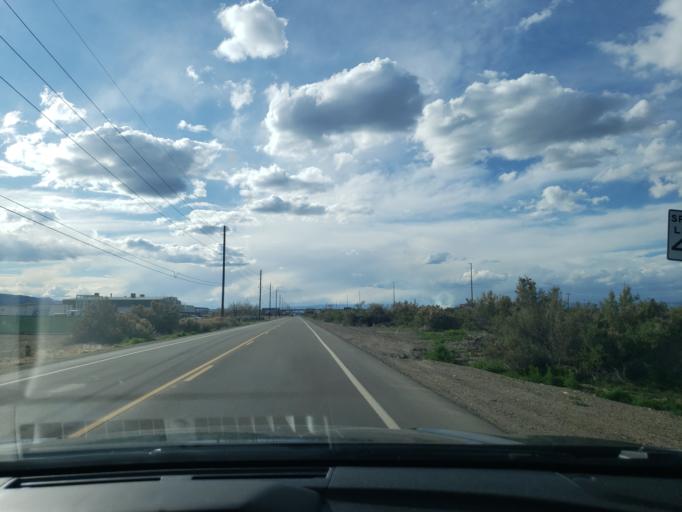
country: US
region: Colorado
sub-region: Mesa County
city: Redlands
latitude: 39.1058
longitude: -108.6381
